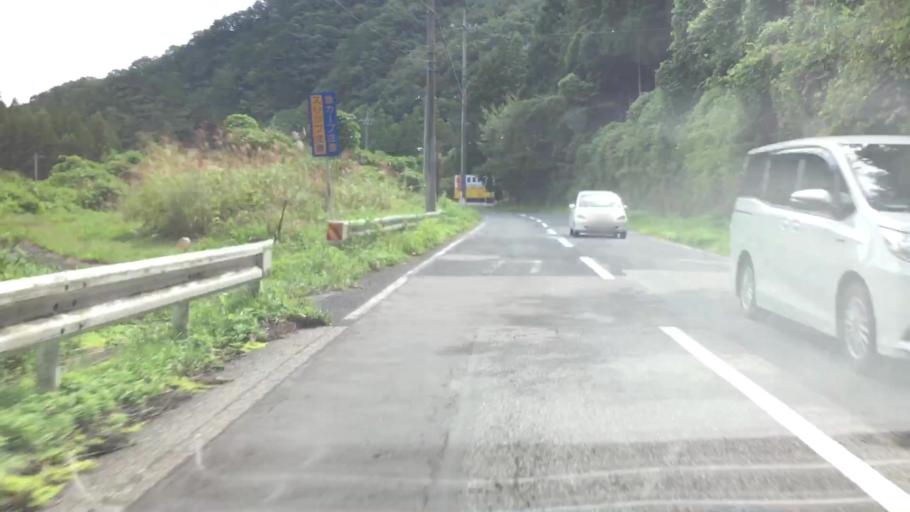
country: JP
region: Tochigi
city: Imaichi
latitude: 36.7607
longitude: 139.6661
